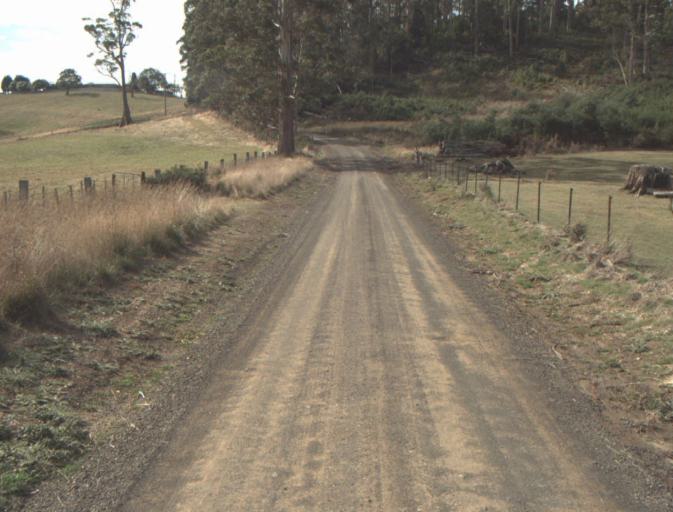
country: AU
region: Tasmania
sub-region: Launceston
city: Mayfield
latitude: -41.1873
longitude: 147.1910
